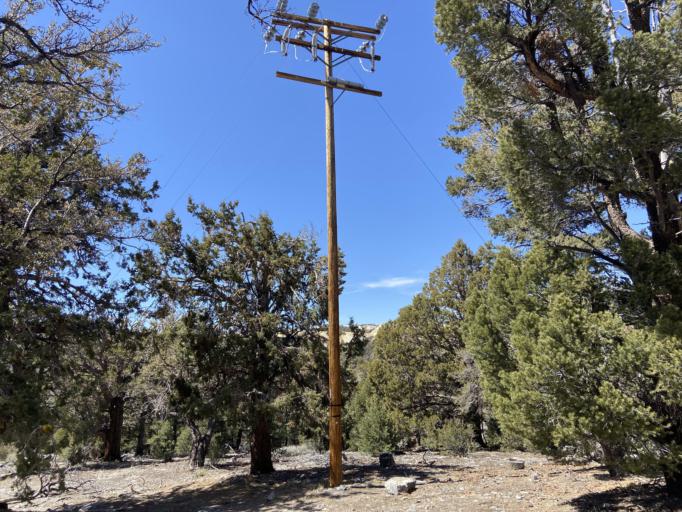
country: US
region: California
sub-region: San Bernardino County
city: Big Bear Lake
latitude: 34.3232
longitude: -116.9288
